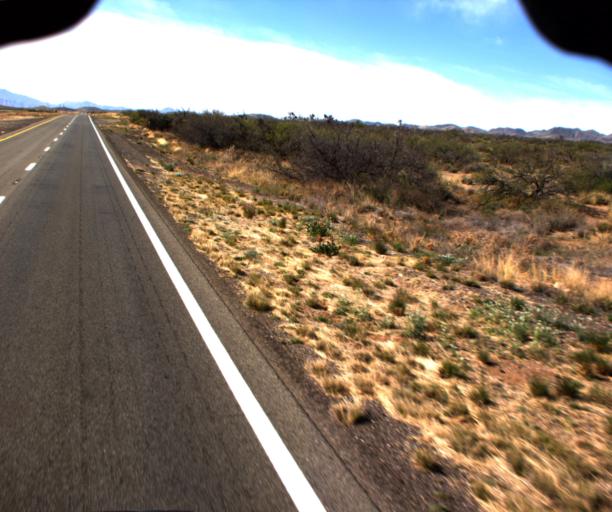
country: US
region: Arizona
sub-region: Graham County
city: Swift Trail Junction
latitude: 32.5024
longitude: -109.6742
